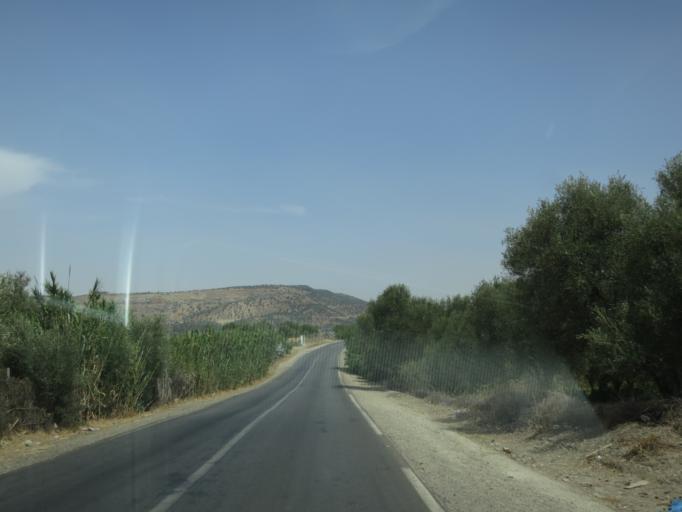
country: MA
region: Meknes-Tafilalet
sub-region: Meknes
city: Meknes
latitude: 34.0455
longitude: -5.5645
